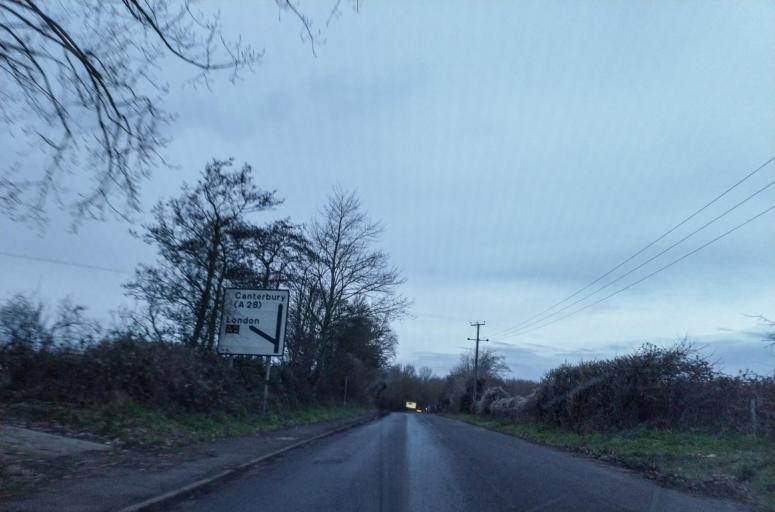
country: GB
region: England
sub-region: Kent
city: Canterbury
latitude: 51.2525
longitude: 1.1181
